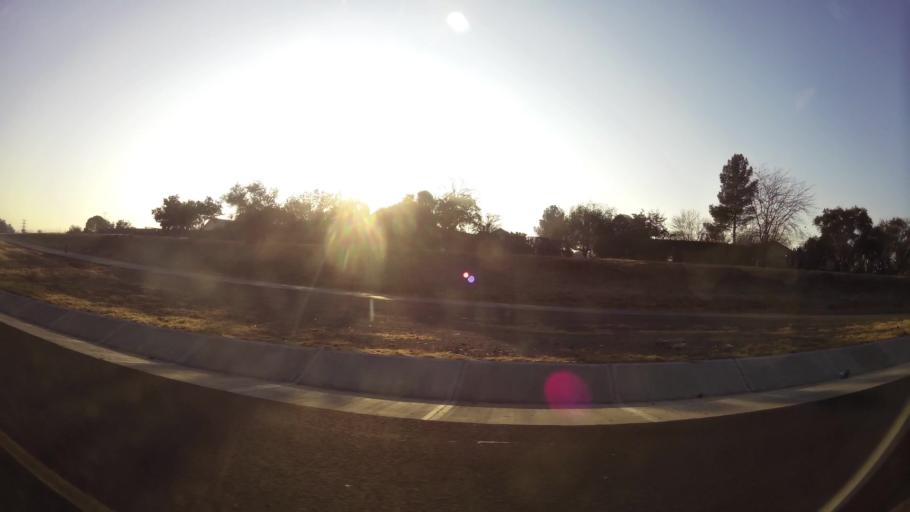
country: ZA
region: Orange Free State
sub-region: Mangaung Metropolitan Municipality
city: Bloemfontein
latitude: -29.1298
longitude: 26.1644
